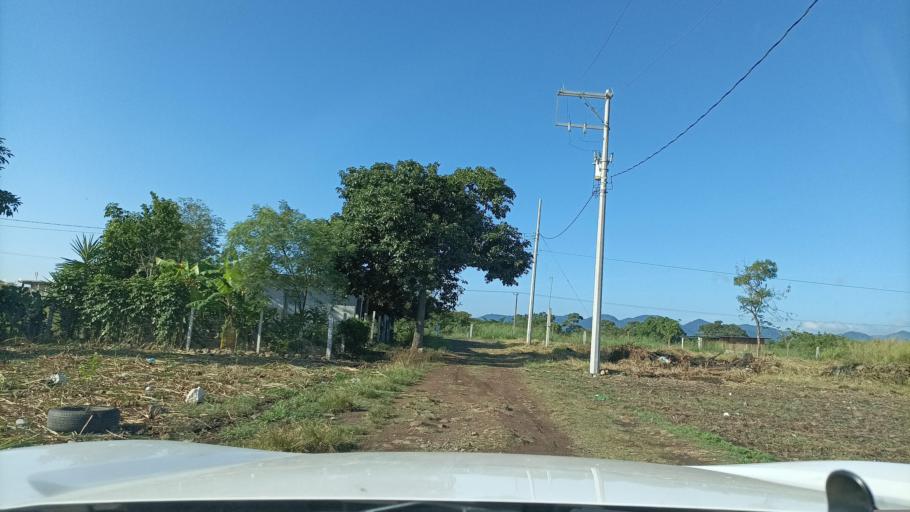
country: MX
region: Veracruz
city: Paso del Macho
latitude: 18.9803
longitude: -96.7301
